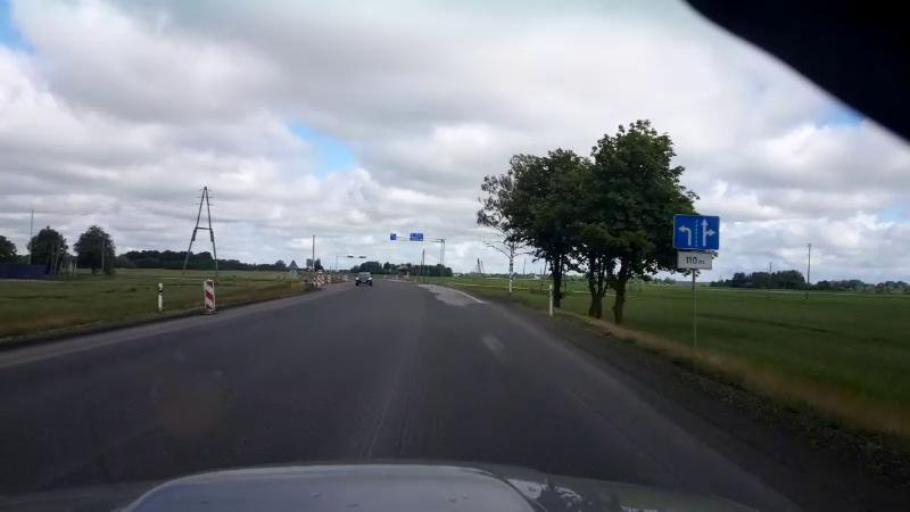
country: LV
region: Bauskas Rajons
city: Bauska
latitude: 56.2906
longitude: 24.3537
